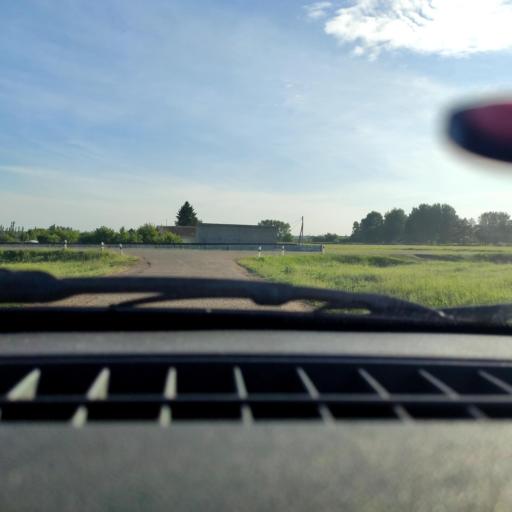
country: RU
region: Bashkortostan
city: Tolbazy
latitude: 54.2952
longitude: 55.8076
